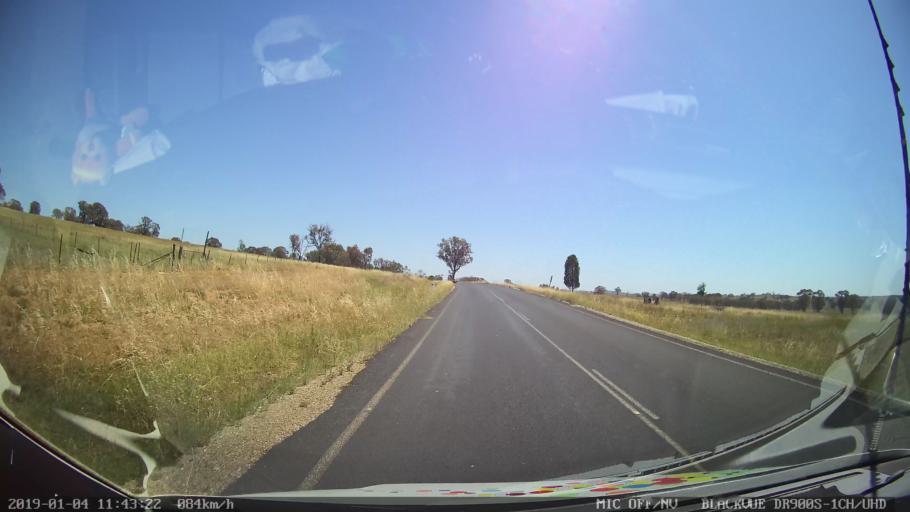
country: AU
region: New South Wales
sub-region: Cabonne
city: Molong
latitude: -32.9699
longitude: 148.7841
